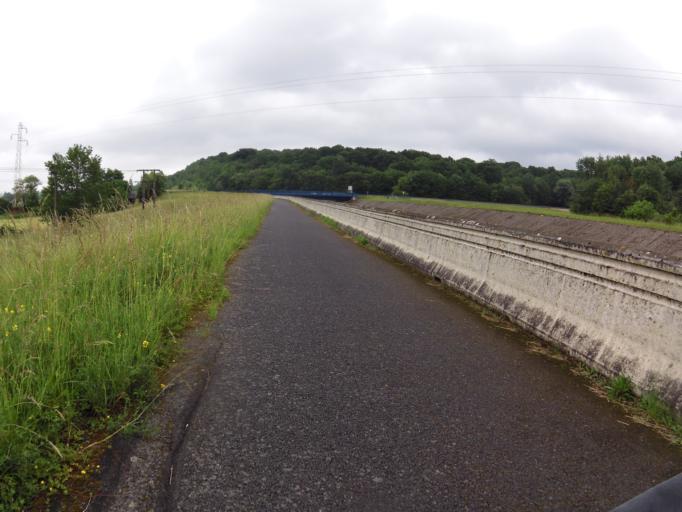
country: FR
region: Champagne-Ardenne
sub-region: Departement de la Haute-Marne
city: Saint-Dizier
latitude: 48.6160
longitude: 4.9148
